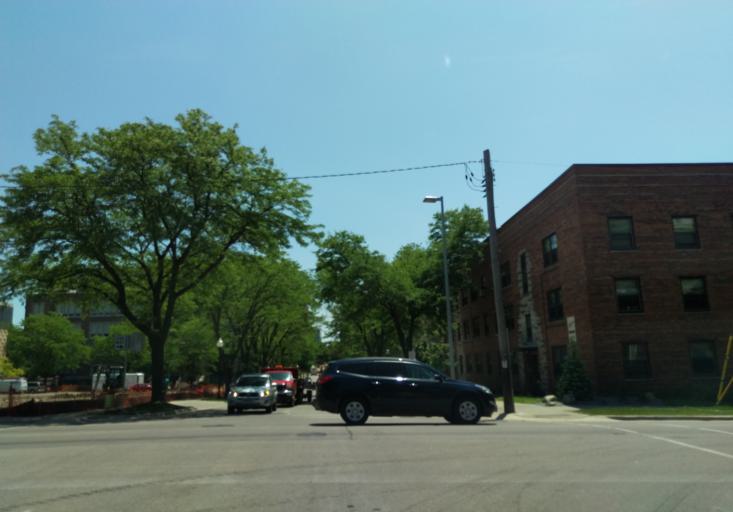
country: US
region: Wisconsin
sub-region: Dane County
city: Madison
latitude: 43.0768
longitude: -89.3891
